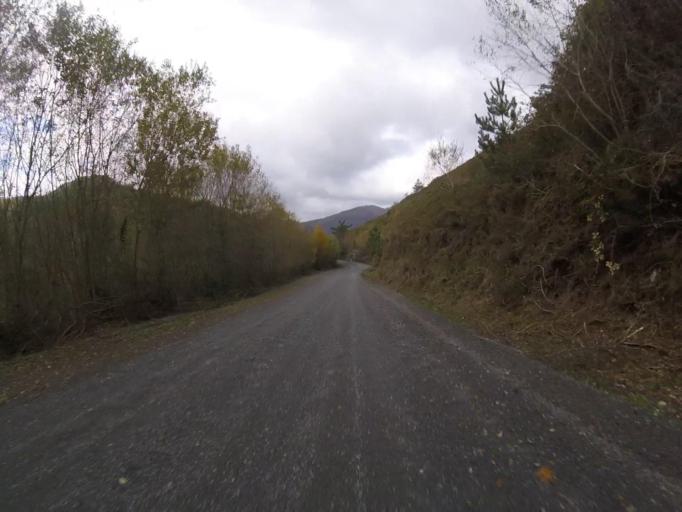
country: ES
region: Navarre
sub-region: Provincia de Navarra
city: Goizueta
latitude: 43.2180
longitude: -1.8295
